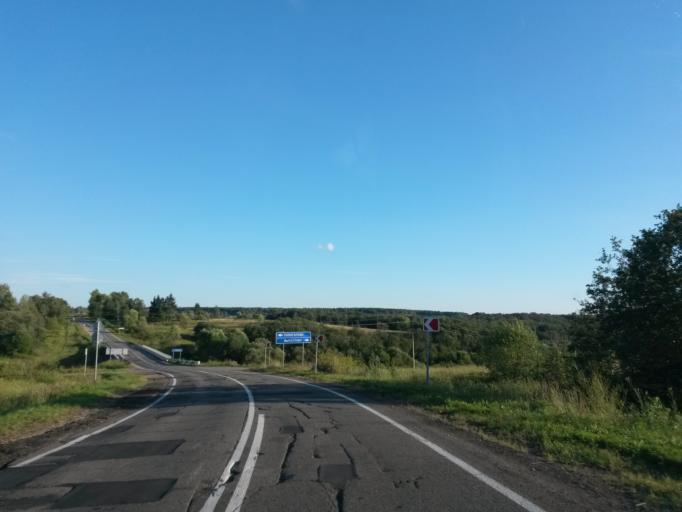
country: RU
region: Jaroslavl
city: Tutayev
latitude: 57.9429
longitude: 39.4954
